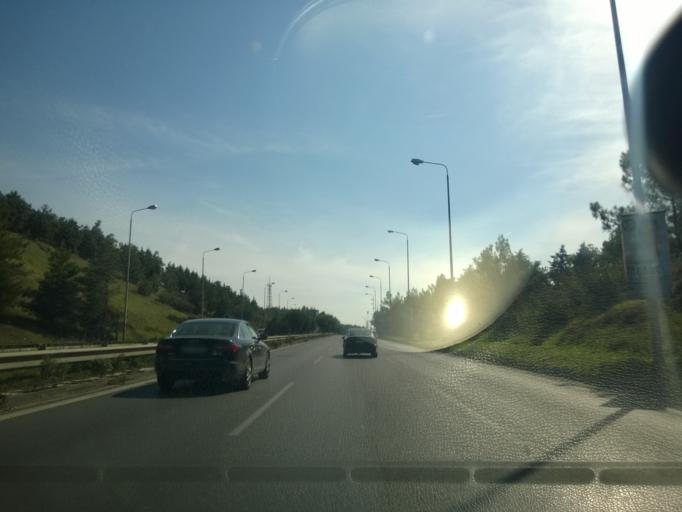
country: GR
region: Central Macedonia
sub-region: Nomos Thessalonikis
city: Agios Pavlos
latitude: 40.6469
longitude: 22.9680
